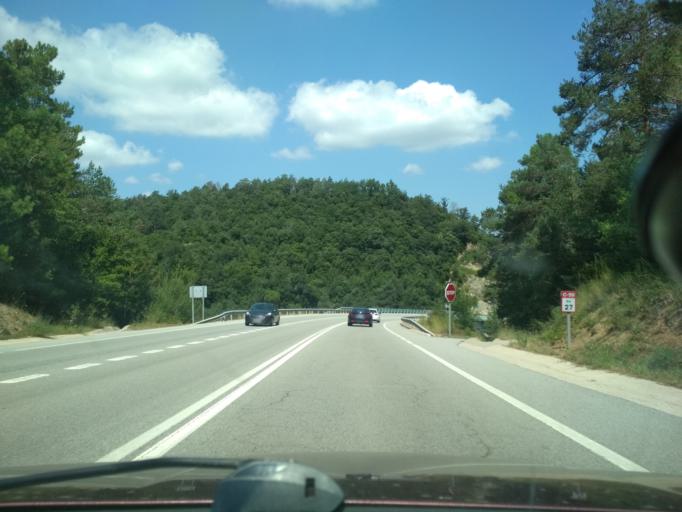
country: ES
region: Catalonia
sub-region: Provincia de Barcelona
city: Sant Quirze Safaja
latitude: 41.7218
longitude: 2.1475
